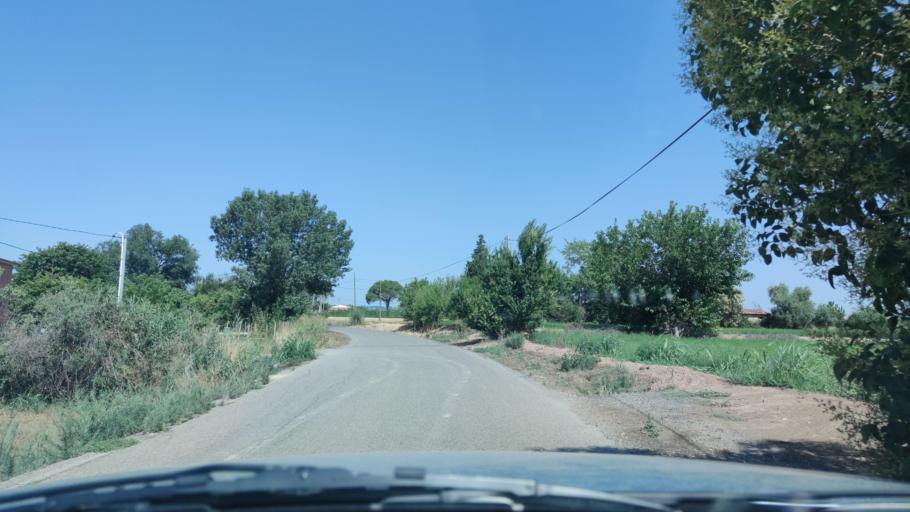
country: ES
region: Catalonia
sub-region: Provincia de Lleida
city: Lleida
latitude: 41.6370
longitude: 0.5944
